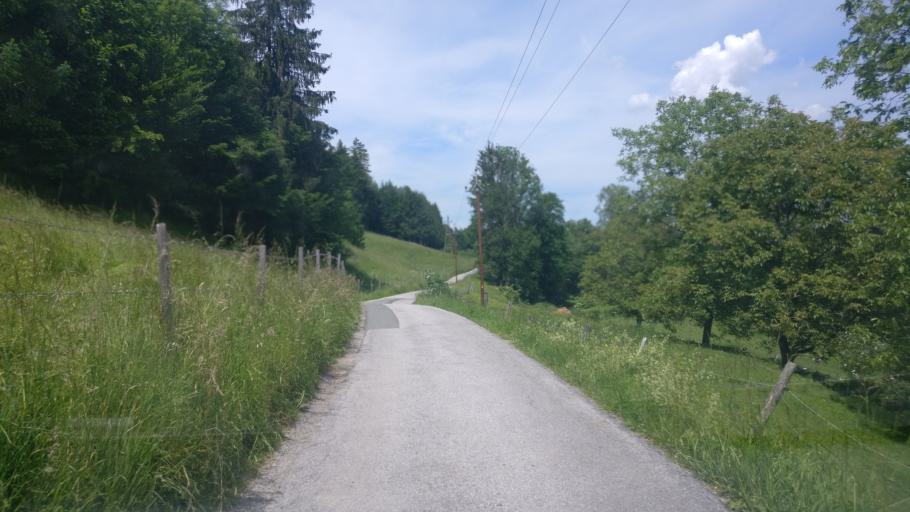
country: AT
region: Salzburg
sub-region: Politischer Bezirk Hallein
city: Kuchl
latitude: 47.6474
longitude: 13.1211
